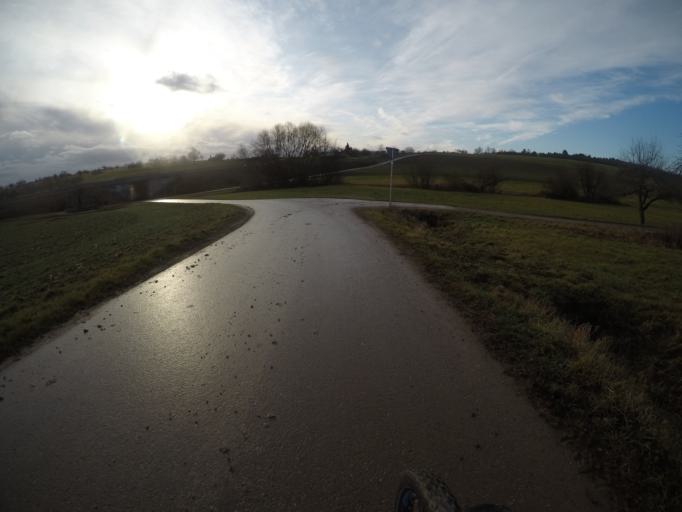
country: DE
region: Baden-Wuerttemberg
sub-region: Regierungsbezirk Stuttgart
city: Unterensingen
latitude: 48.6616
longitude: 9.3418
